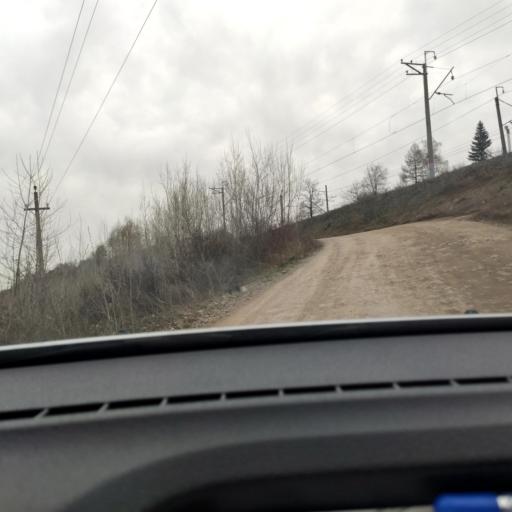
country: RU
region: Bashkortostan
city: Avdon
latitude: 54.6070
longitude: 55.6088
